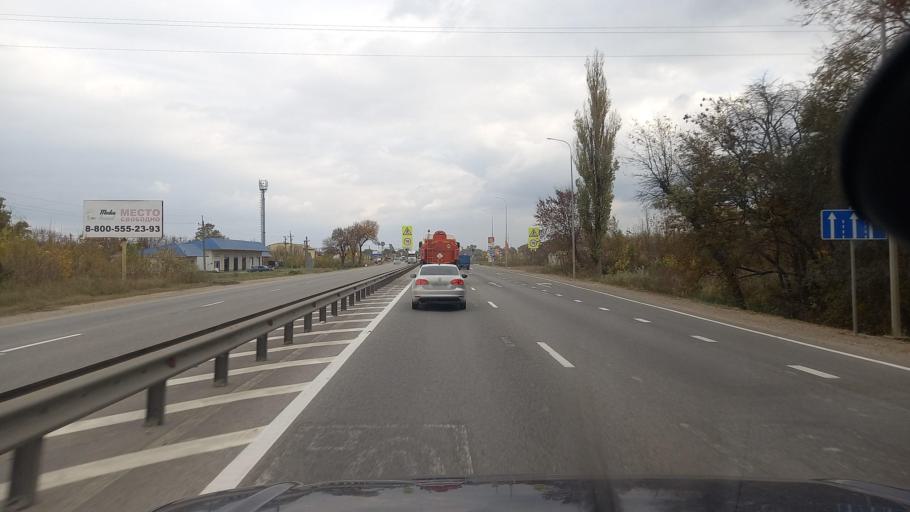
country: RU
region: Adygeya
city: Enem
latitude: 44.9074
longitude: 38.8794
